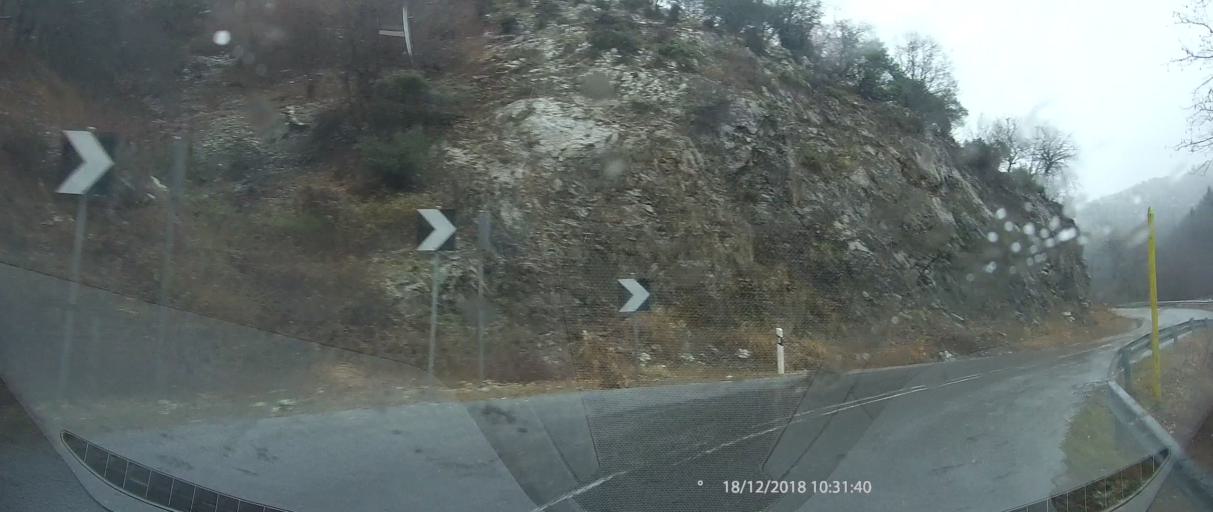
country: GR
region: Central Macedonia
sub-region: Nomos Pierias
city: Kato Milia
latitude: 40.1923
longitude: 22.2855
